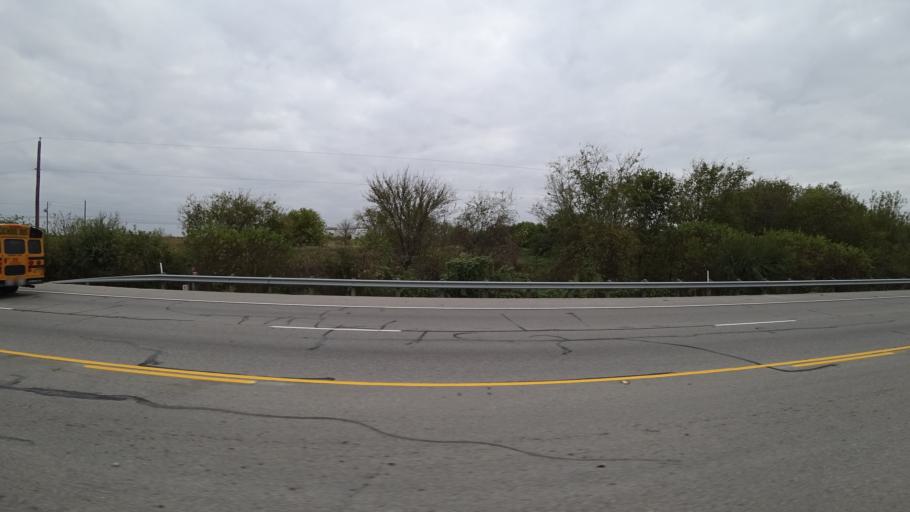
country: US
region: Texas
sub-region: Travis County
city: Windemere
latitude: 30.4470
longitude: -97.6421
